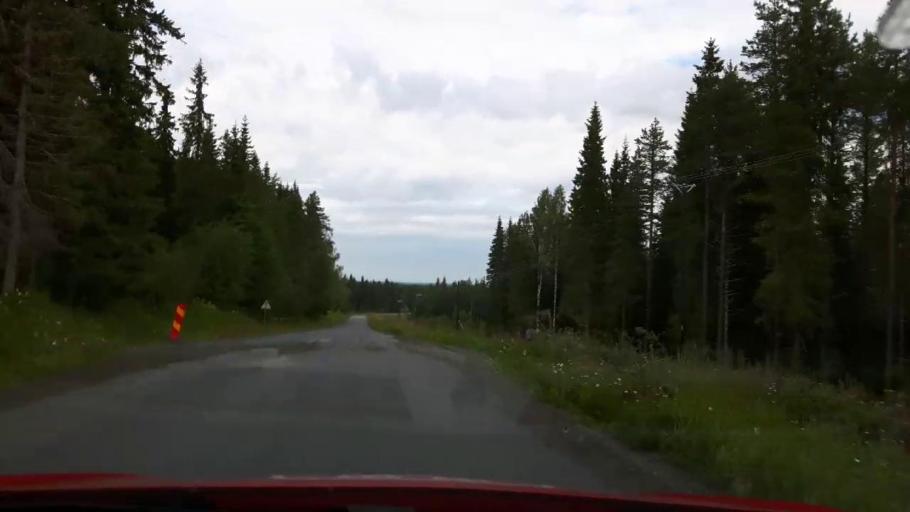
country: SE
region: Jaemtland
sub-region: Stroemsunds Kommun
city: Stroemsund
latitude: 63.5294
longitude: 15.3579
